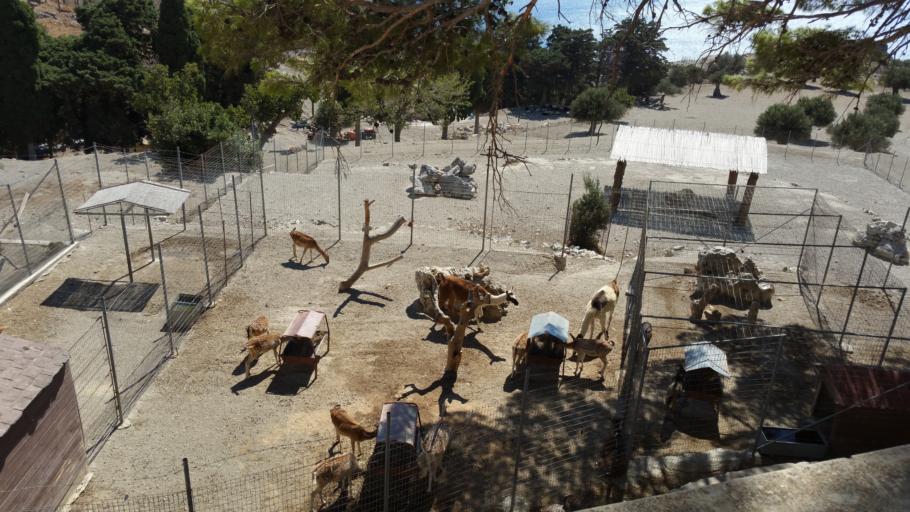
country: GR
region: Crete
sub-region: Nomos Rethymnis
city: Atsipopoulon
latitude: 35.1574
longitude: 24.4562
